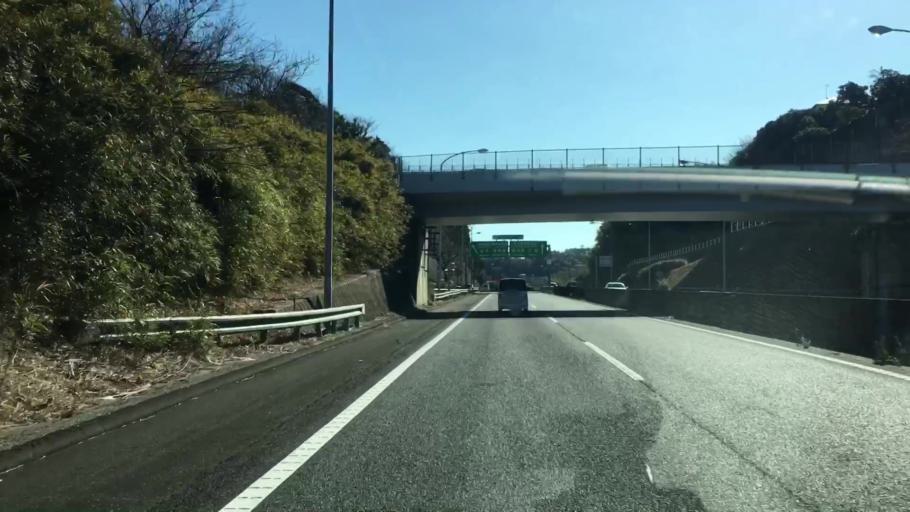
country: JP
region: Kanagawa
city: Kamakura
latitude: 35.3688
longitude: 139.5953
